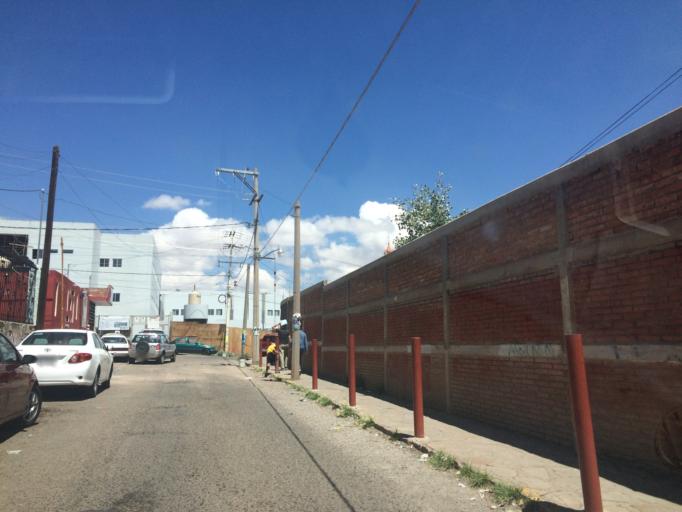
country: MX
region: Zacatecas
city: Zacatecas
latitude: 22.7644
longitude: -102.5762
